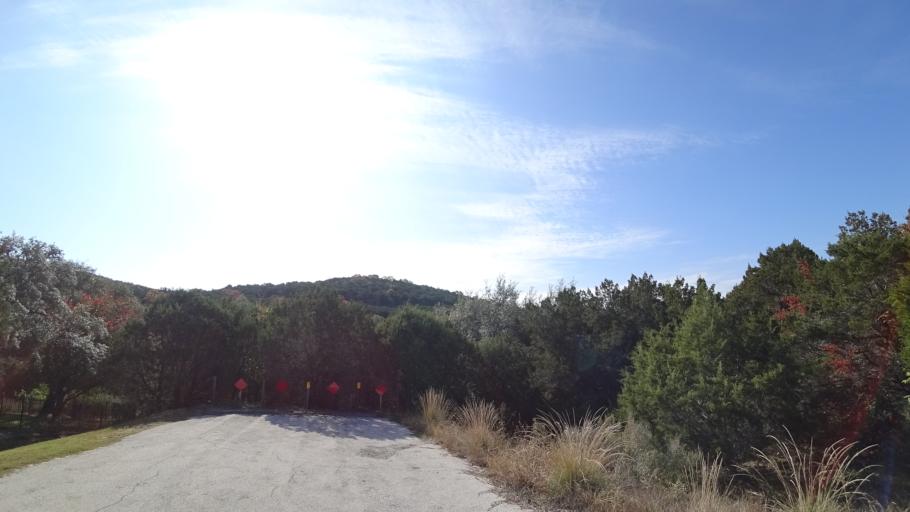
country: US
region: Texas
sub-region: Travis County
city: West Lake Hills
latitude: 30.3708
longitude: -97.8157
